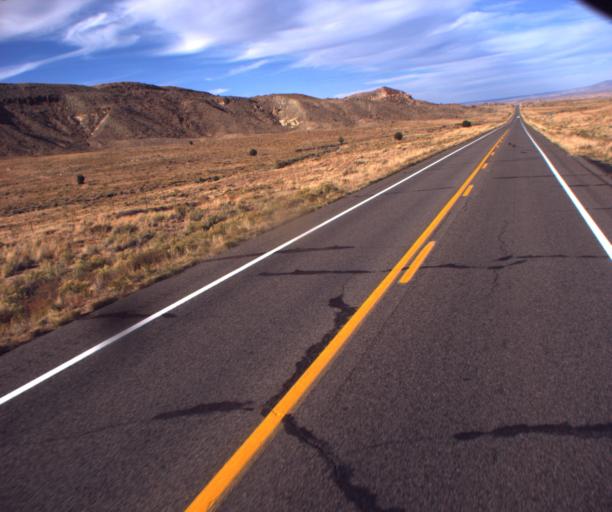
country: US
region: New Mexico
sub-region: San Juan County
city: Shiprock
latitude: 36.9296
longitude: -109.0808
